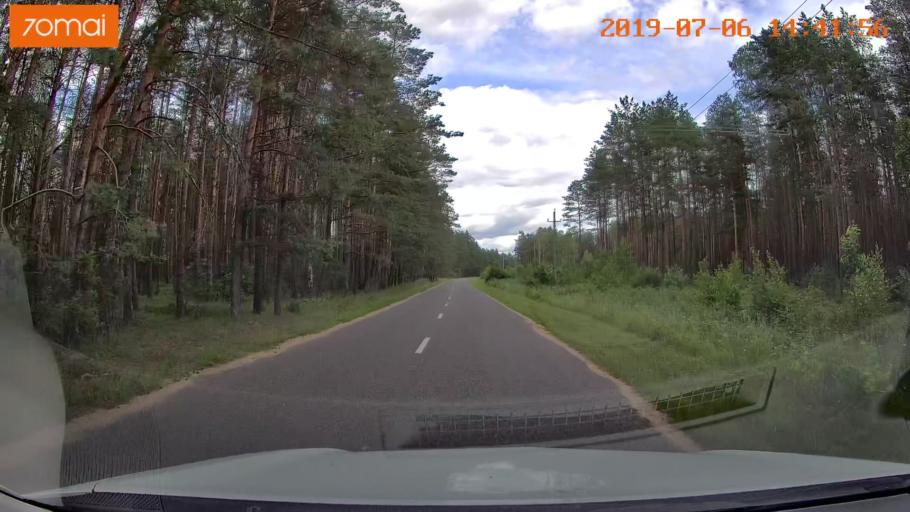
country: BY
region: Minsk
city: Ivyanyets
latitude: 53.9368
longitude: 26.6831
